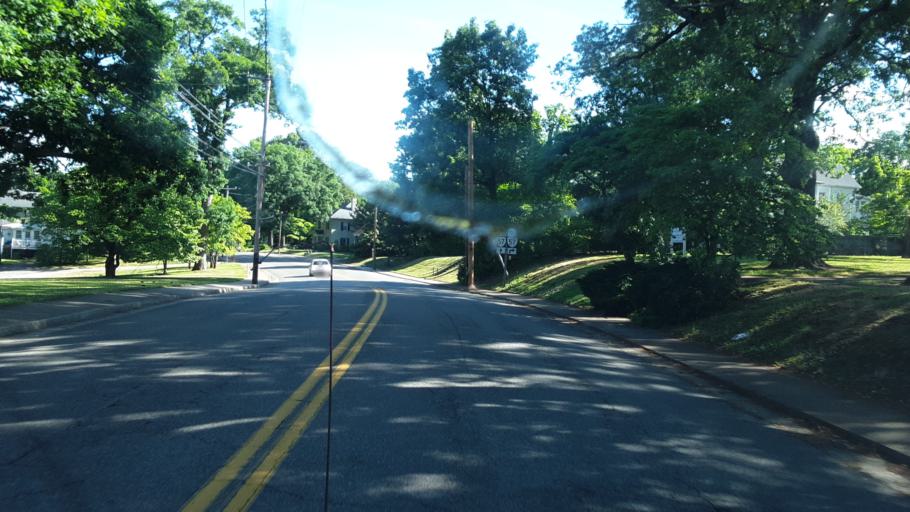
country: US
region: Virginia
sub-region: Pittsylvania County
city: Chatham
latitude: 36.8199
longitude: -79.3964
